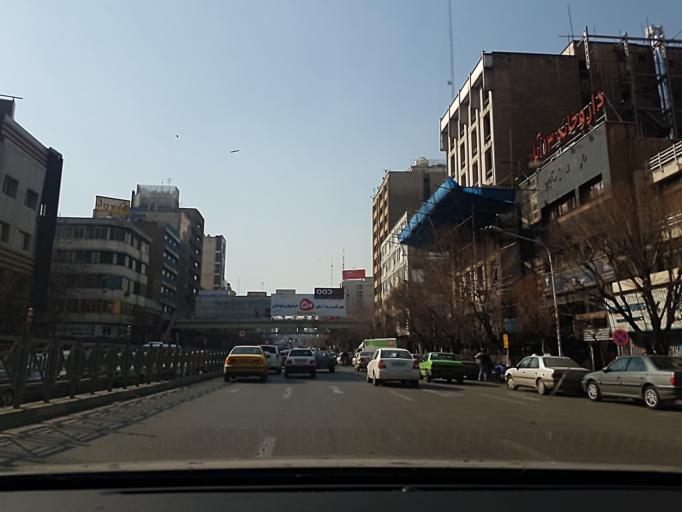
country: IR
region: Tehran
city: Tehran
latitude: 35.7154
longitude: 51.4225
